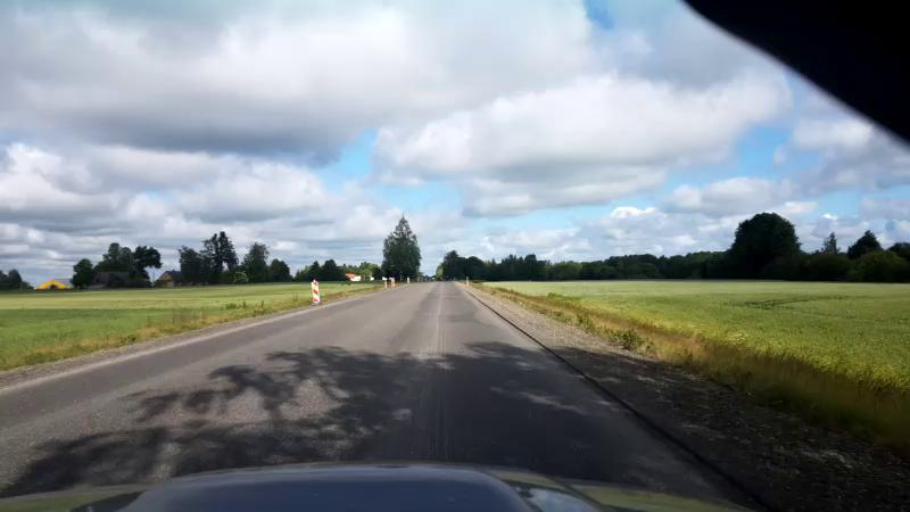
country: LV
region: Bauskas Rajons
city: Bauska
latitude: 56.3181
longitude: 24.3237
